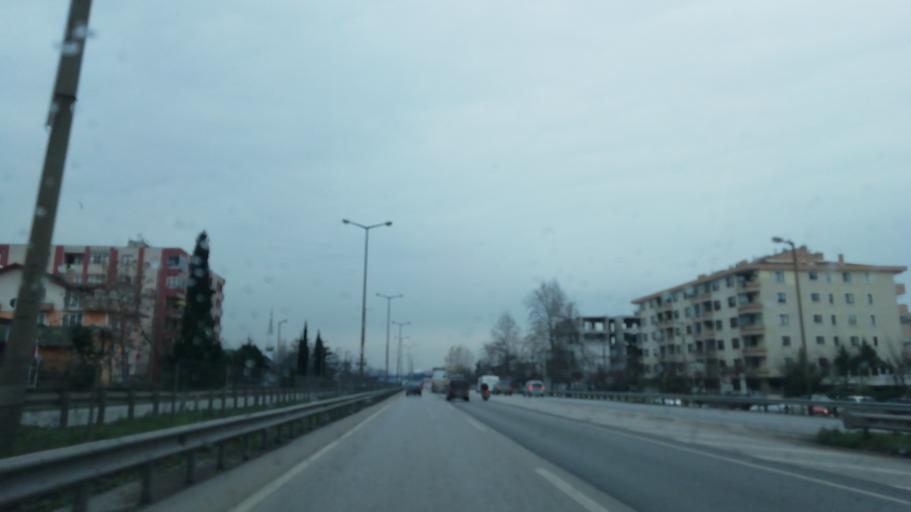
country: TR
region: Kocaeli
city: Izmit
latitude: 40.7630
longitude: 29.8800
